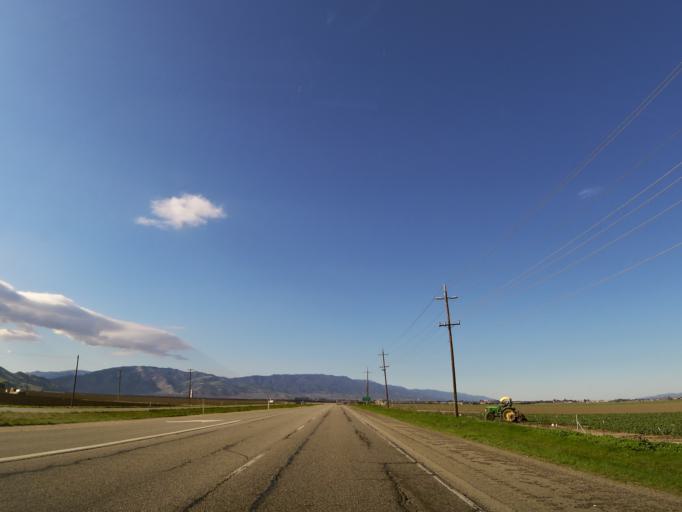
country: US
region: California
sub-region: Monterey County
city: Greenfield
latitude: 36.2951
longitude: -121.2044
